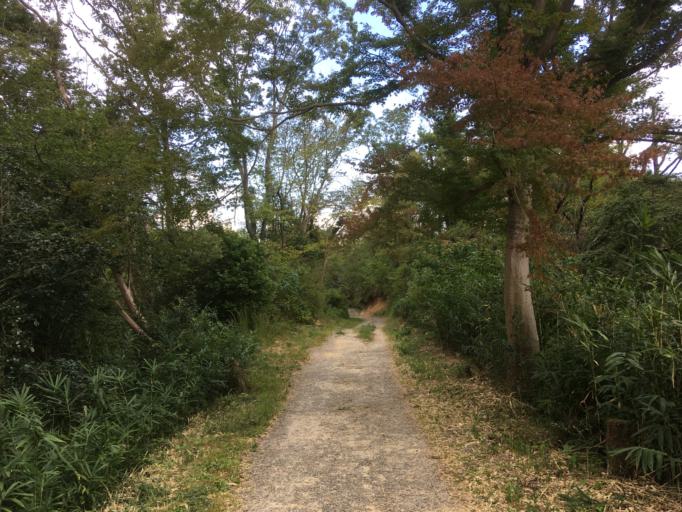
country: JP
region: Osaka
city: Daitocho
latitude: 34.7247
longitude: 135.6700
